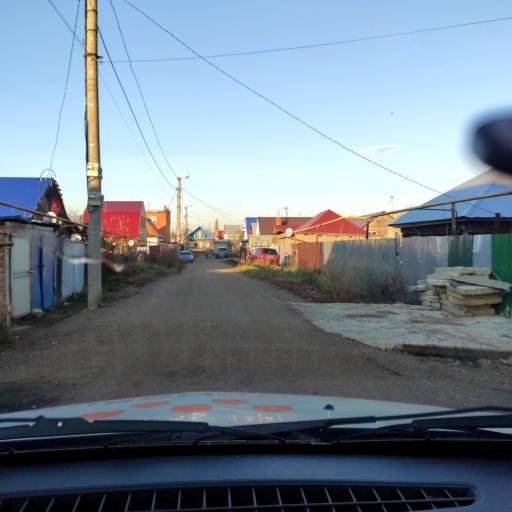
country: RU
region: Bashkortostan
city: Ufa
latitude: 54.7741
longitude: 56.0525
